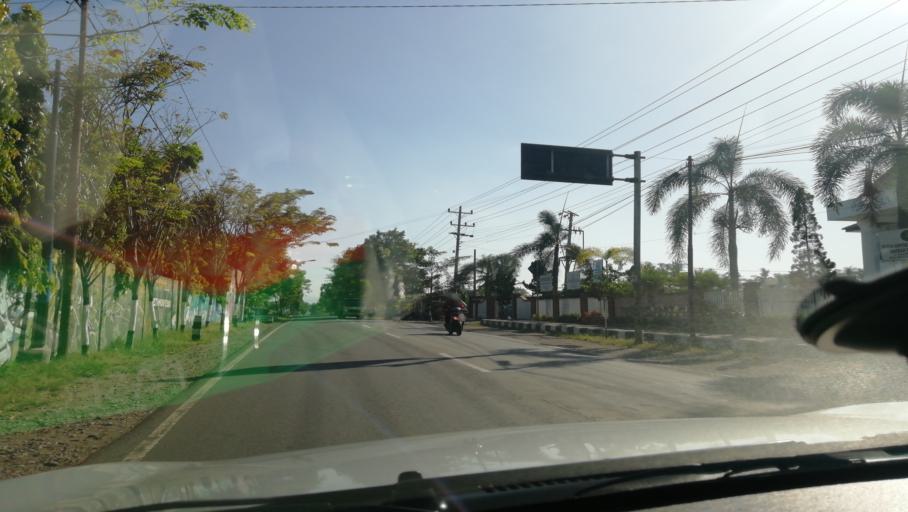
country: ID
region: Central Java
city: Kutoarjo
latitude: -7.7266
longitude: 109.9720
